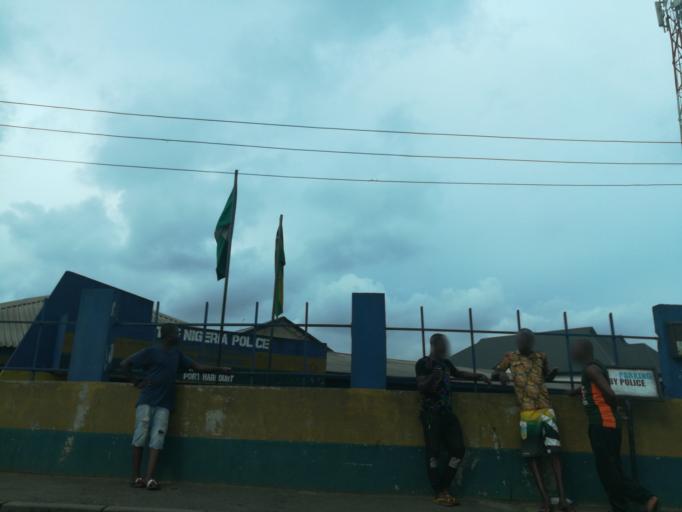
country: NG
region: Rivers
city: Port Harcourt
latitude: 4.8059
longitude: 6.9888
